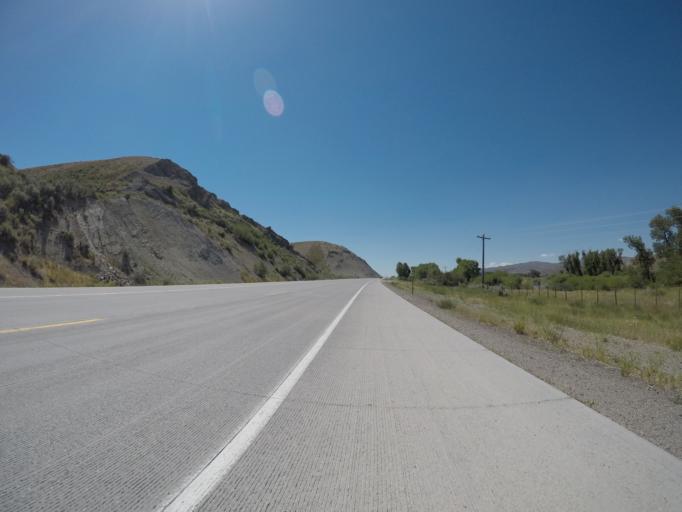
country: US
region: Idaho
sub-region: Bear Lake County
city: Montpelier
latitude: 42.1302
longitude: -110.9685
